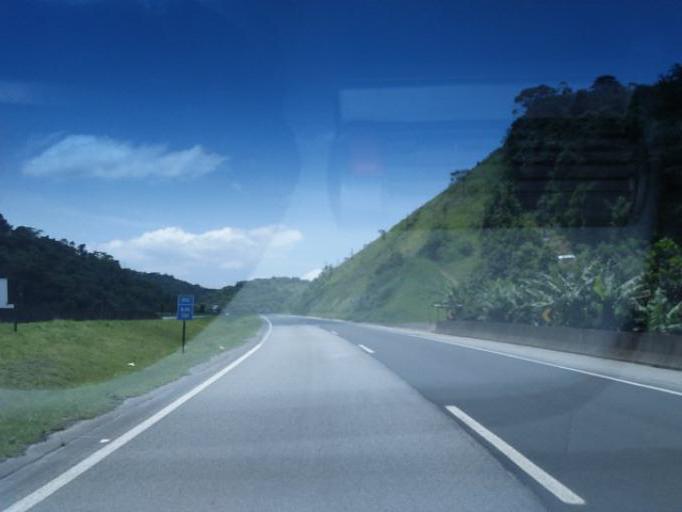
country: BR
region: Sao Paulo
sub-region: Miracatu
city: Miracatu
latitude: -24.2269
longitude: -47.3639
